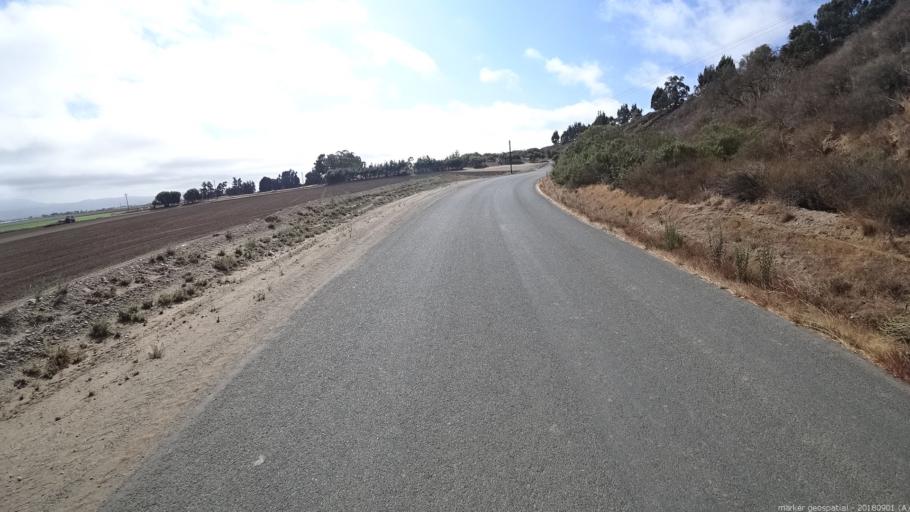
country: US
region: California
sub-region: Monterey County
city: Soledad
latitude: 36.3965
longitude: -121.3710
